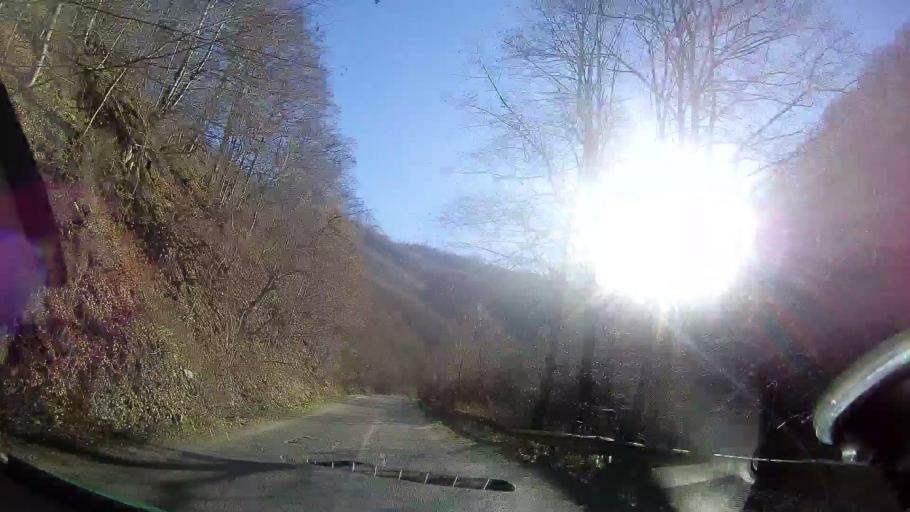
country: RO
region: Cluj
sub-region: Comuna Sacueu
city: Sacuieu
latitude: 46.8417
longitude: 22.8618
